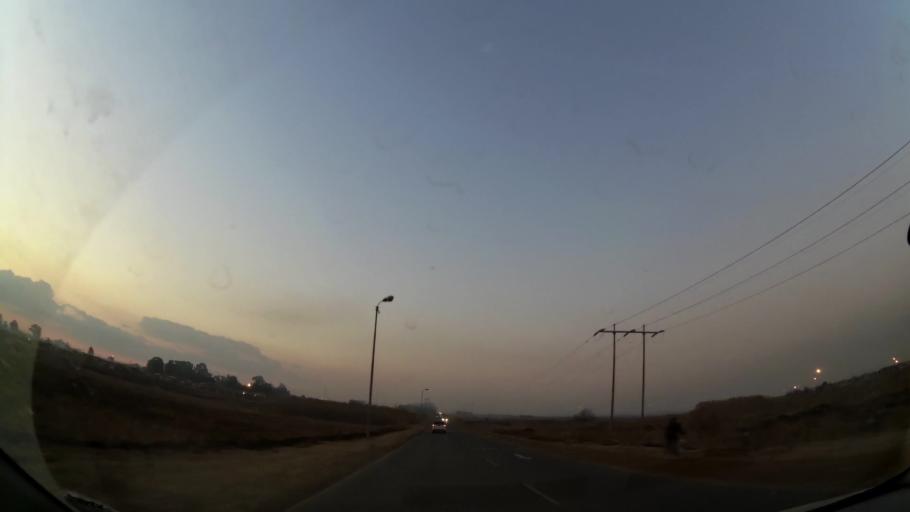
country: ZA
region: Gauteng
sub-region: Ekurhuleni Metropolitan Municipality
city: Springs
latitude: -26.3238
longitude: 28.3754
